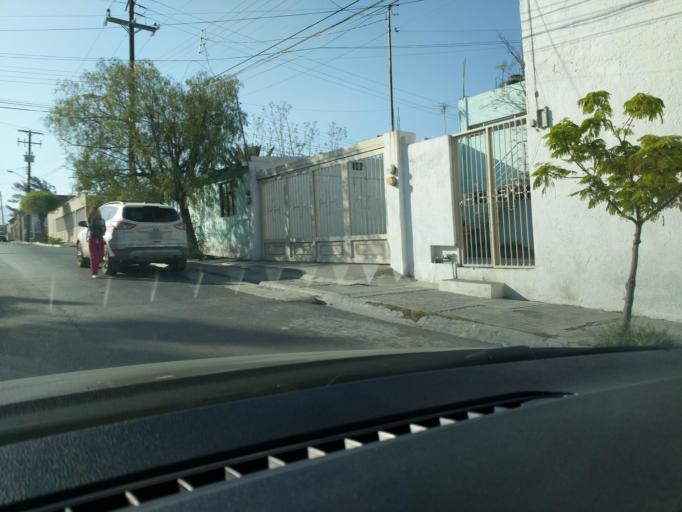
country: MX
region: Coahuila
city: Saltillo
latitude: 25.4624
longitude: -100.9845
